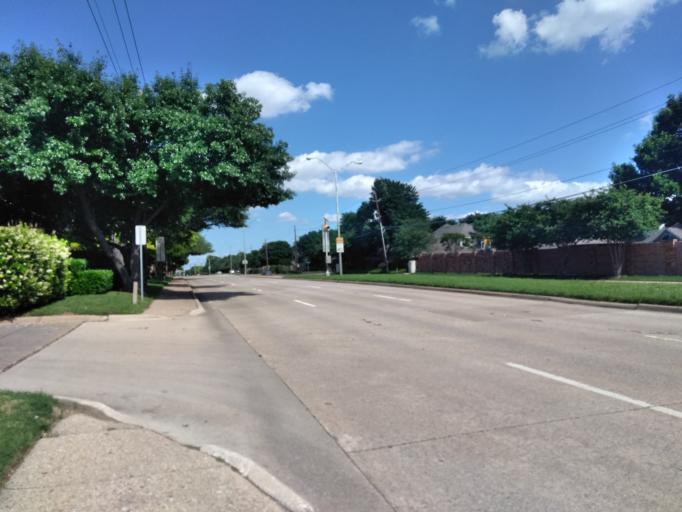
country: US
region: Texas
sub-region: Dallas County
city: Addison
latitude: 32.9983
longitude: -96.8041
